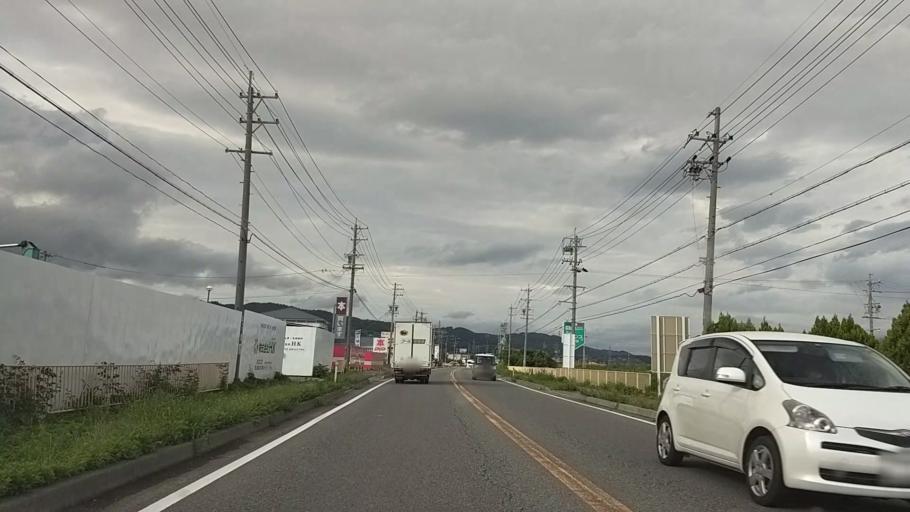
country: JP
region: Nagano
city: Suzaka
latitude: 36.6926
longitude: 138.2687
